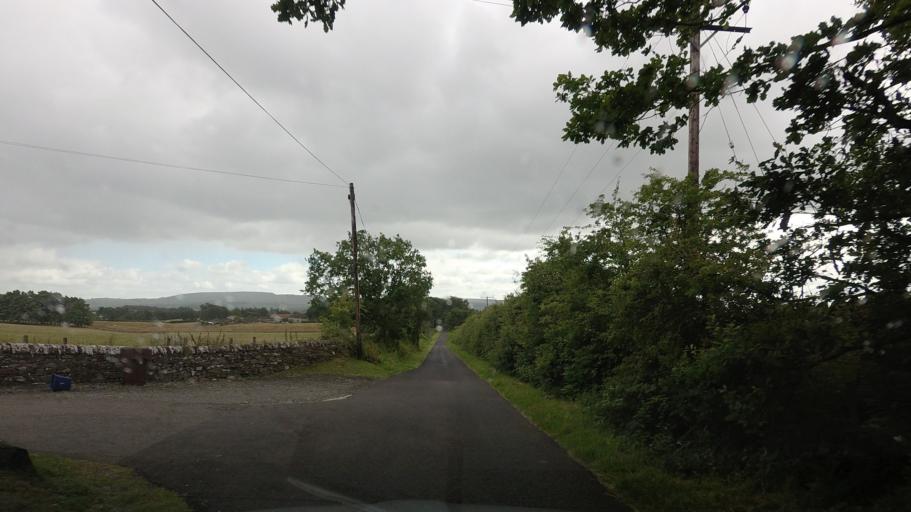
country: GB
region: Scotland
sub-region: Stirling
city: Killearn
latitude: 56.0739
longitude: -4.4503
